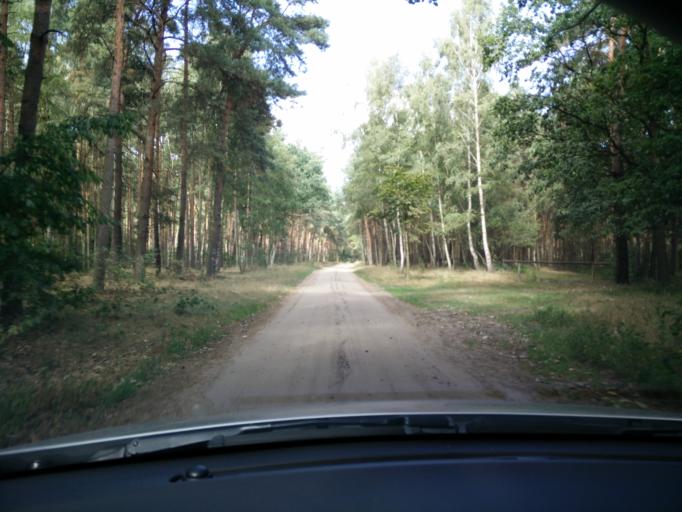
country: PL
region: Greater Poland Voivodeship
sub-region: Powiat sredzki
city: Sroda Wielkopolska
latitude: 52.2821
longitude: 17.2433
